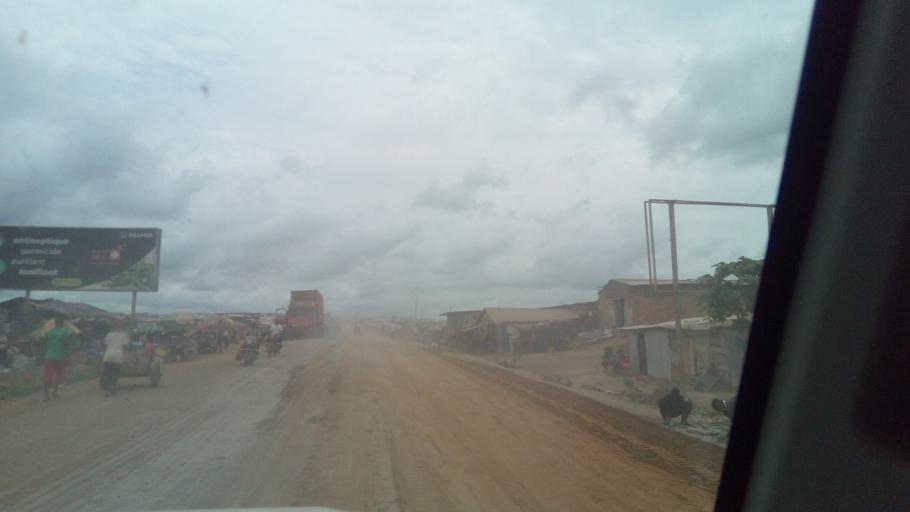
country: AO
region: Zaire
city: Mbanza Congo
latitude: -5.8386
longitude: 14.0758
